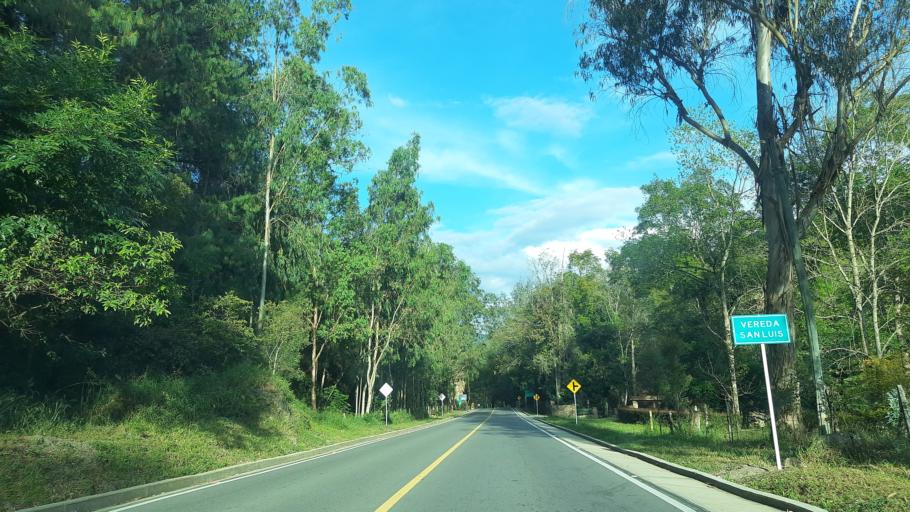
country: CO
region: Cundinamarca
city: Macheta
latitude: 5.0730
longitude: -73.5895
